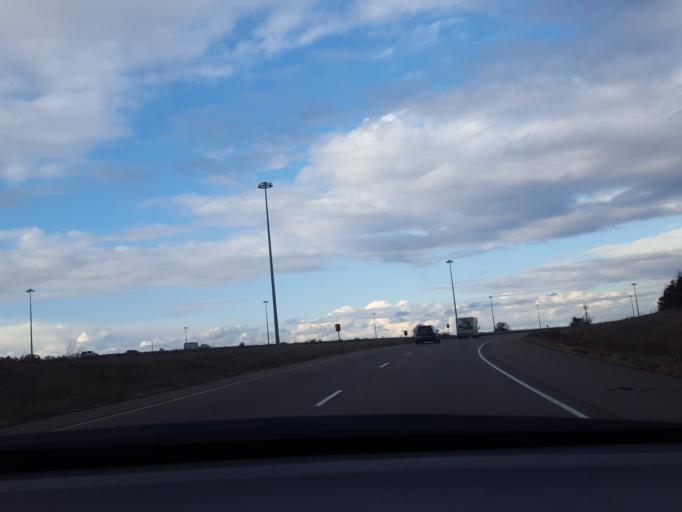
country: CA
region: Ontario
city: Mississauga
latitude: 43.6371
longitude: -79.6533
